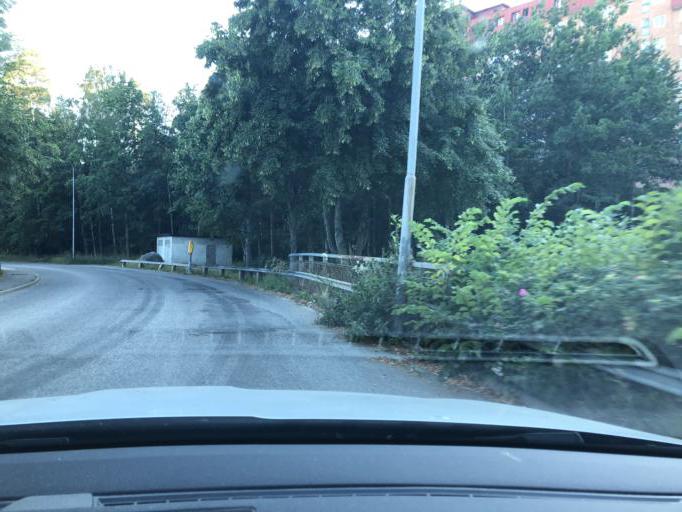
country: SE
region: Stockholm
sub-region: Sodertalje Kommun
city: Soedertaelje
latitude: 59.1797
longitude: 17.6208
